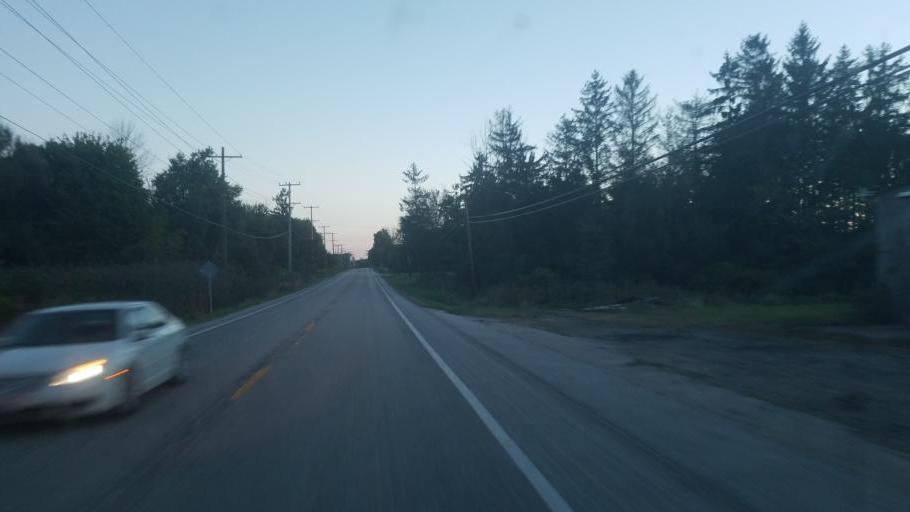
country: US
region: Ohio
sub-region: Ashtabula County
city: Conneaut
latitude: 41.7804
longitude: -80.5721
